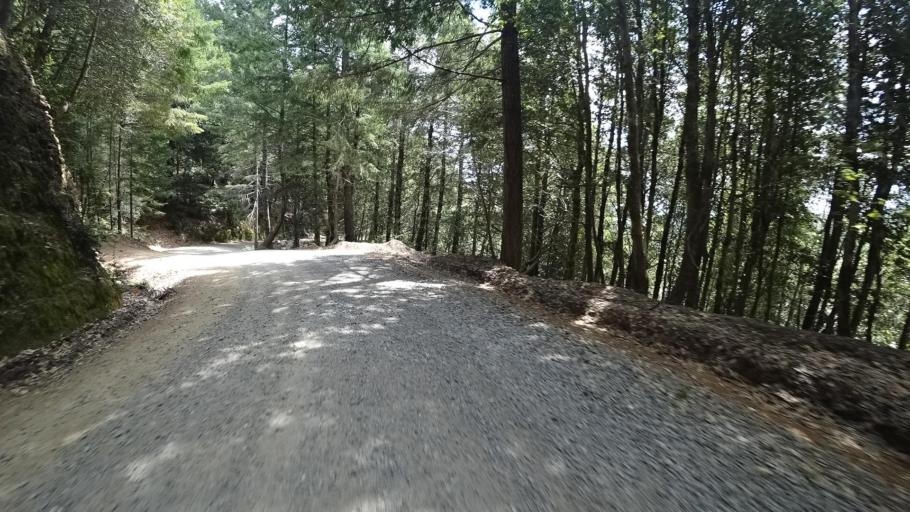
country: US
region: California
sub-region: Humboldt County
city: Redway
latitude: 40.0138
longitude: -123.9878
